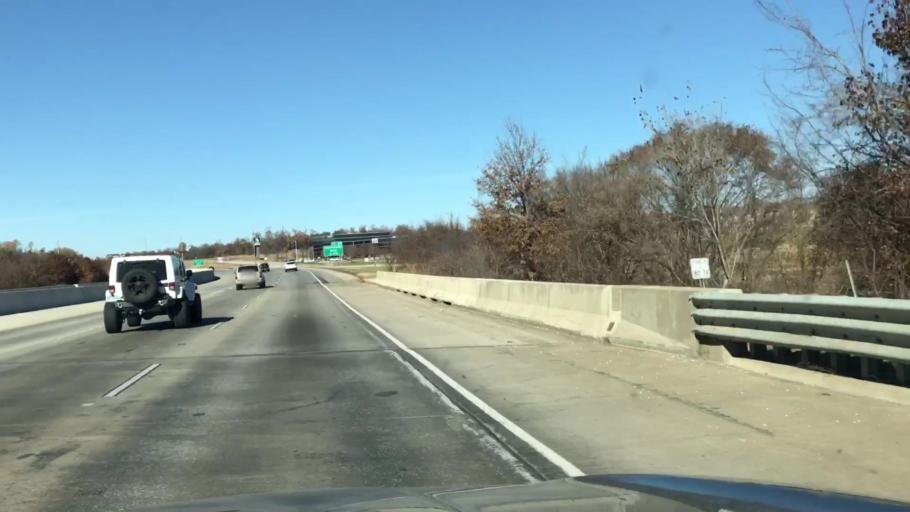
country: US
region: Arkansas
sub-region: Benton County
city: Lowell
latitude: 36.2921
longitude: -94.1628
